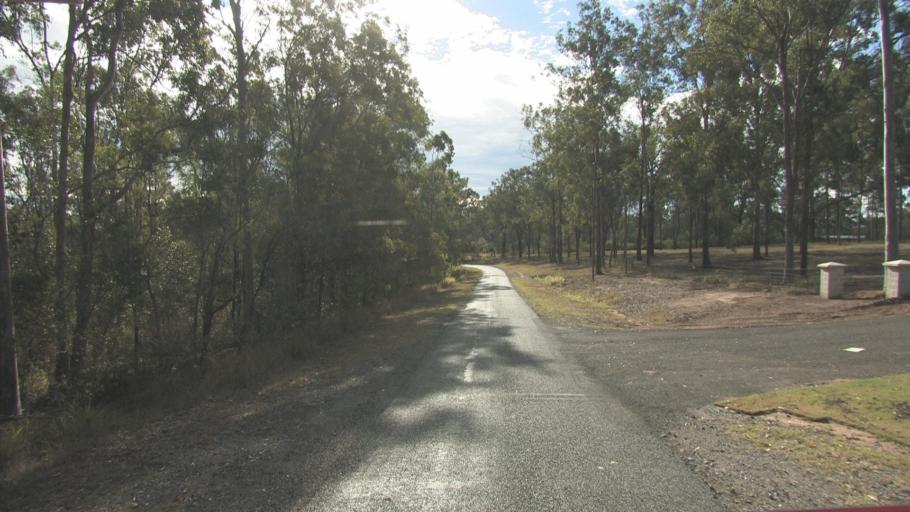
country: AU
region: Queensland
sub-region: Logan
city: Cedar Vale
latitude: -27.8407
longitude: 153.0678
